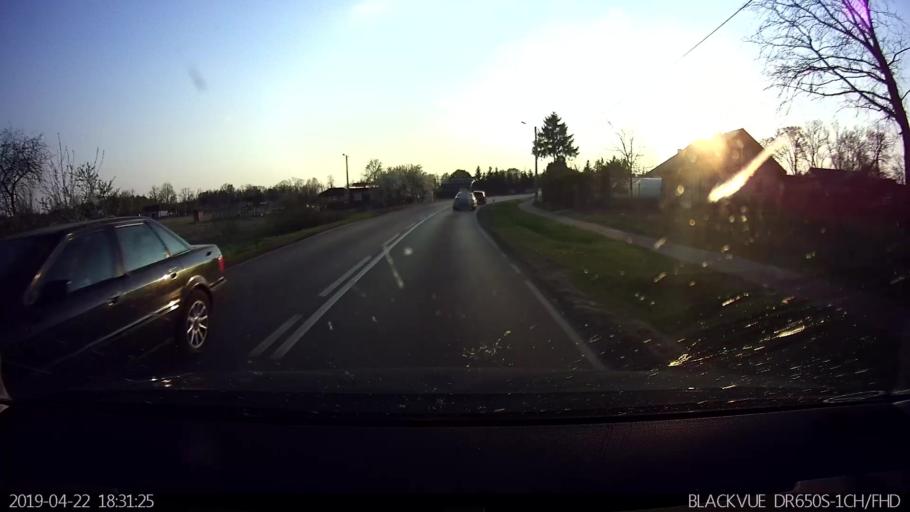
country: PL
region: Masovian Voivodeship
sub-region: Powiat wolominski
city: Tluszcz
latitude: 52.4519
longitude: 21.4187
